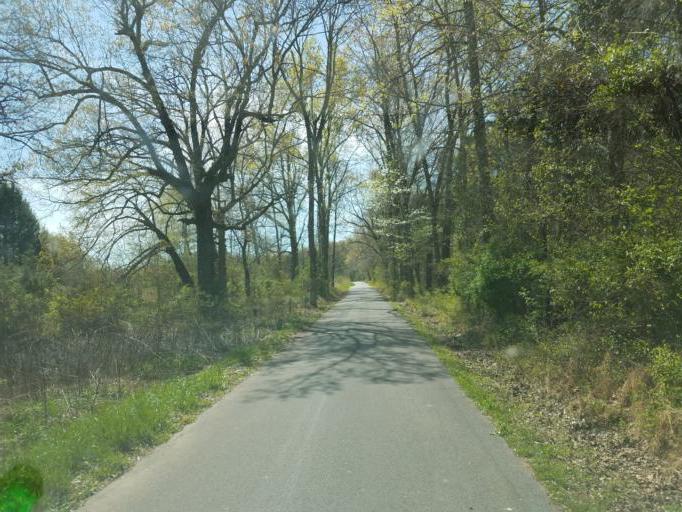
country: US
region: Kentucky
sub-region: Barren County
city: Cave City
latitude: 37.1803
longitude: -86.0481
